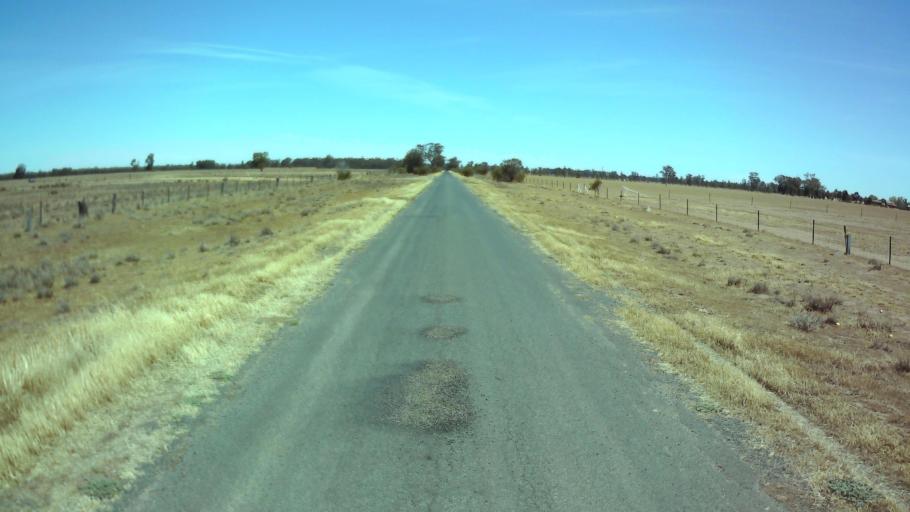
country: AU
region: New South Wales
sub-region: Weddin
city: Grenfell
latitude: -33.8909
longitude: 147.6882
